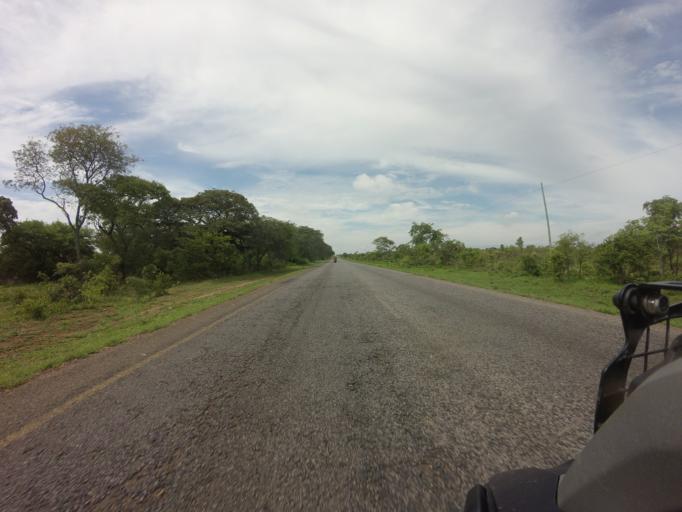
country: ZM
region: Southern
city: Monze
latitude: -16.0952
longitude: 27.5524
